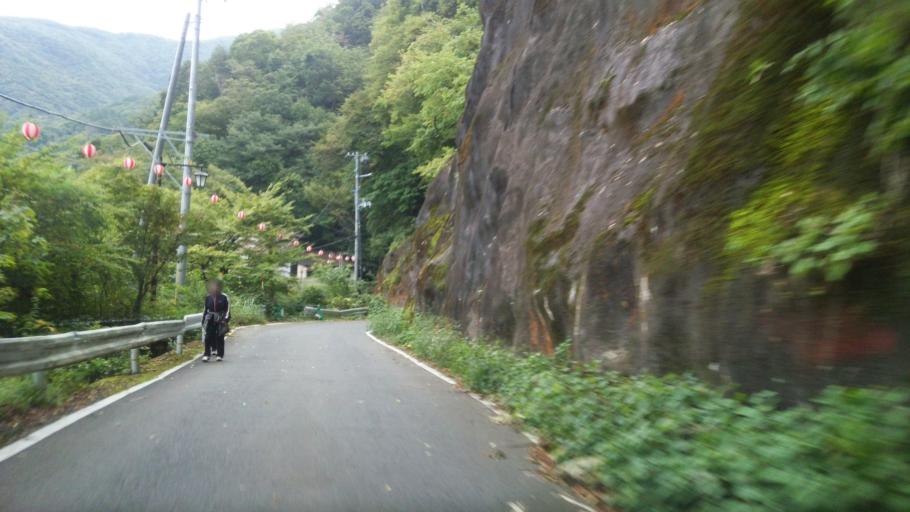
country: JP
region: Fukushima
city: Inawashiro
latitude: 37.3635
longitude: 139.9171
